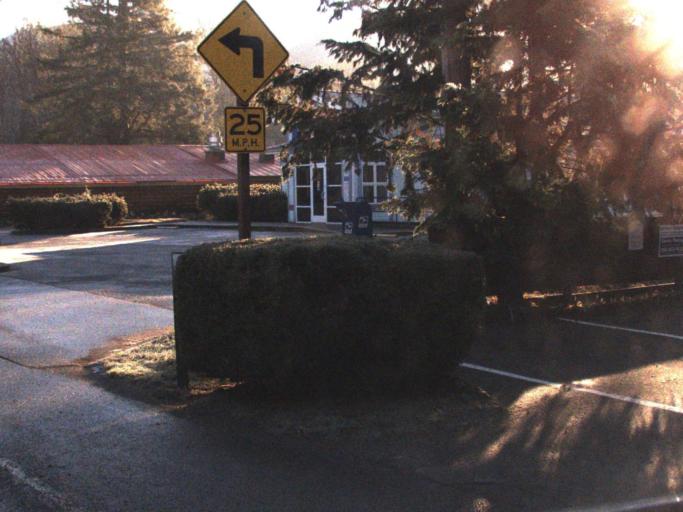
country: US
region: Washington
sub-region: Snohomish County
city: Darrington
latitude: 48.5267
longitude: -121.4333
